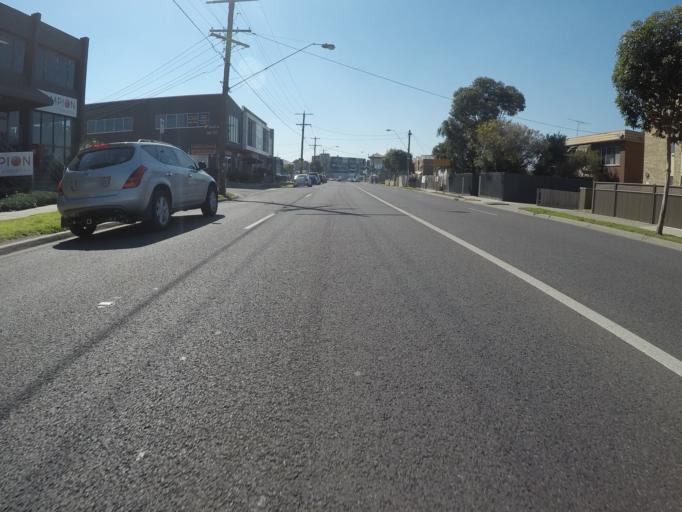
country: AU
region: Victoria
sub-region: Moreland
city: Pascoe Vale
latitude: -37.7451
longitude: 144.9268
